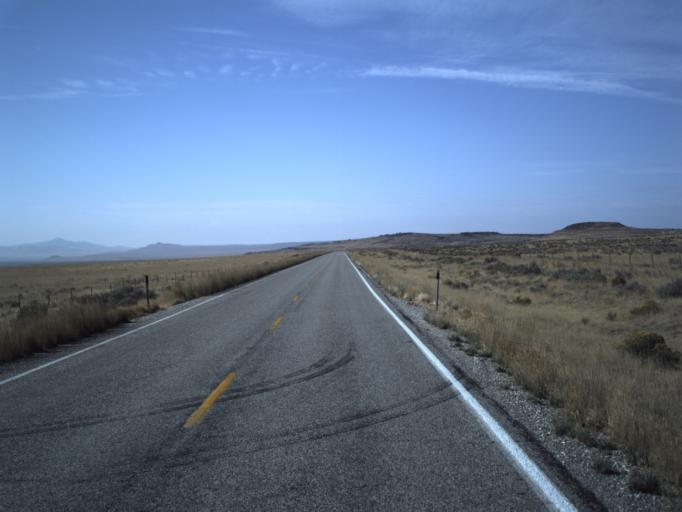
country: US
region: Idaho
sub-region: Minidoka County
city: Rupert
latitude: 41.8623
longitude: -113.1278
